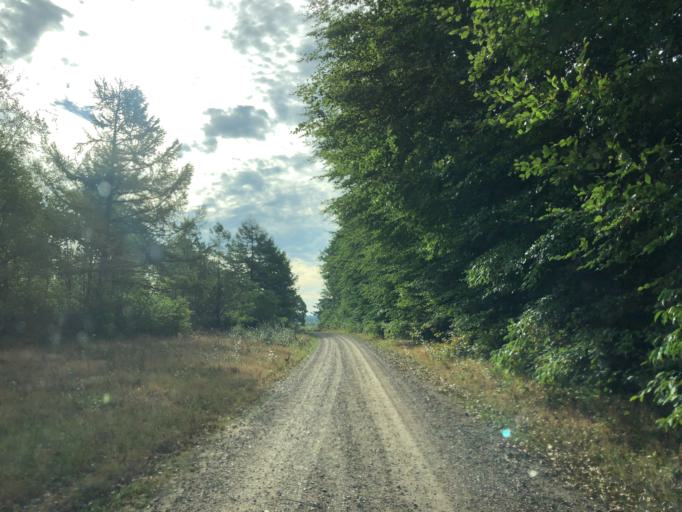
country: DK
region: Central Jutland
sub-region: Holstebro Kommune
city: Ulfborg
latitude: 56.1740
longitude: 8.3713
